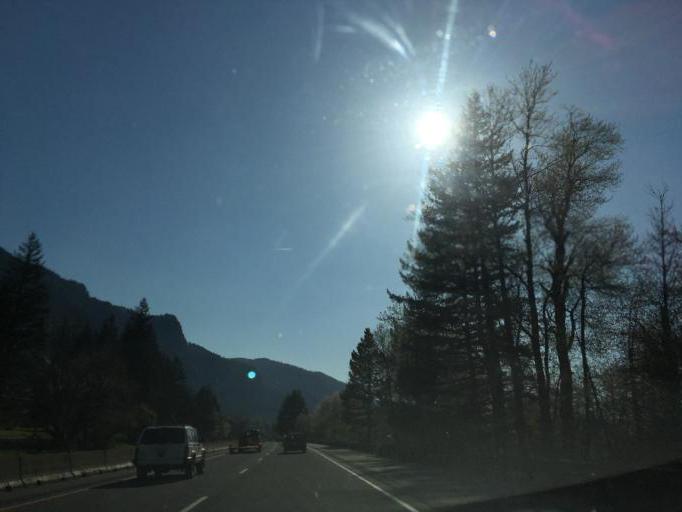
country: US
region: Oregon
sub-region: Hood River County
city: Cascade Locks
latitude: 45.6064
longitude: -122.0361
